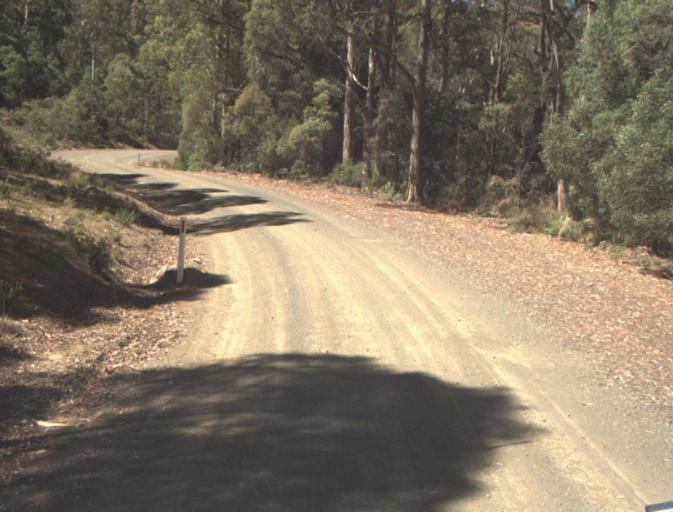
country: AU
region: Tasmania
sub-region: Launceston
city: Newstead
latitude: -41.3032
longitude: 147.3327
